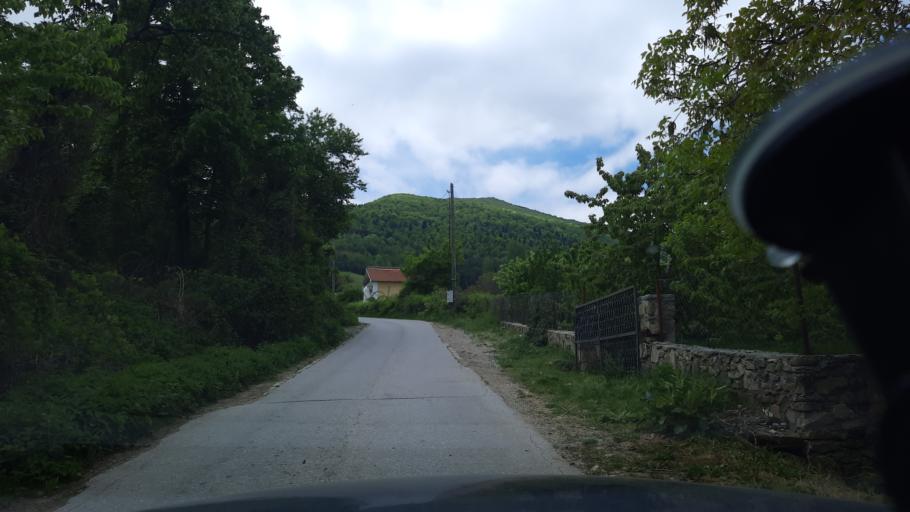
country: MK
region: Bitola
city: Bitola
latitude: 41.0264
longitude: 21.2865
